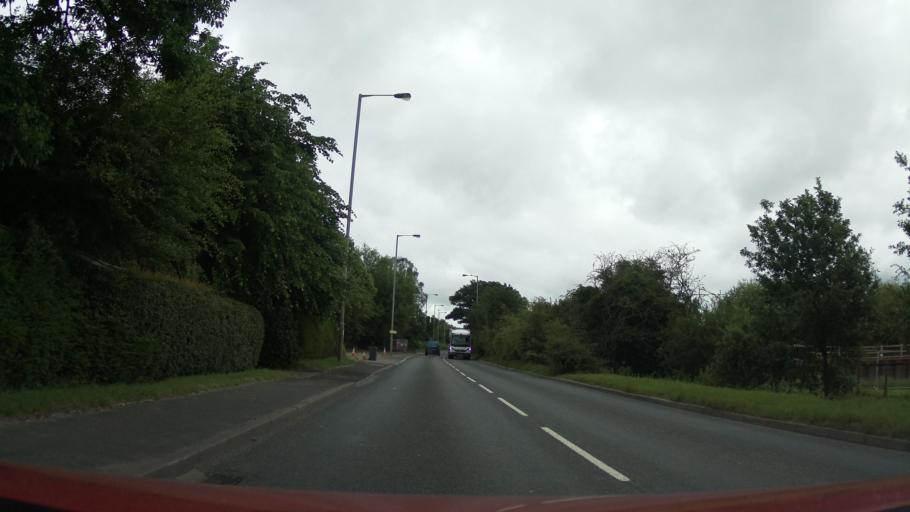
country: GB
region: England
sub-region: Staffordshire
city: Burton upon Trent
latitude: 52.8318
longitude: -1.6140
